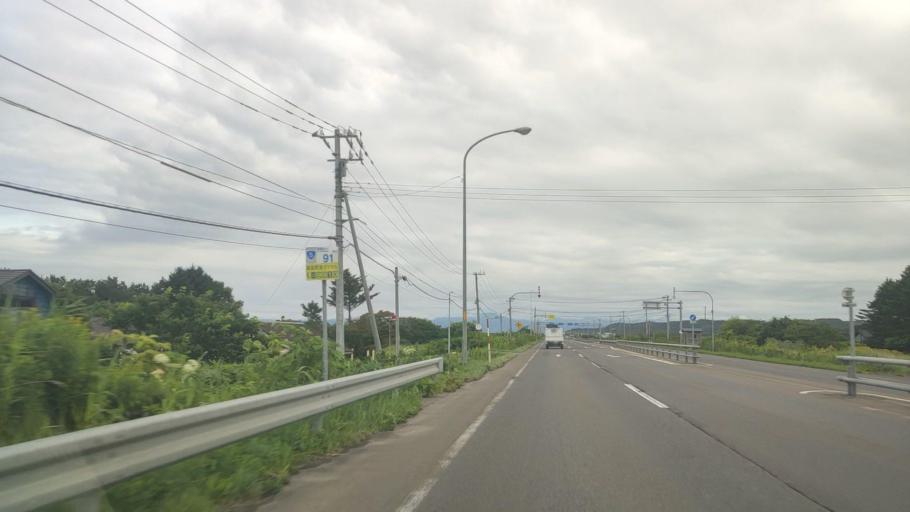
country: JP
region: Hokkaido
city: Niseko Town
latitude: 42.4064
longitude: 140.3054
